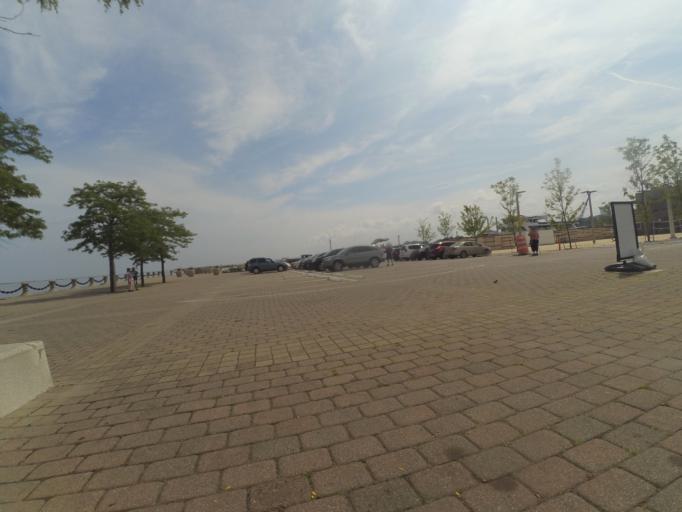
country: US
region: Ohio
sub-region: Cuyahoga County
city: Cleveland
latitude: 41.5109
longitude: -81.6971
